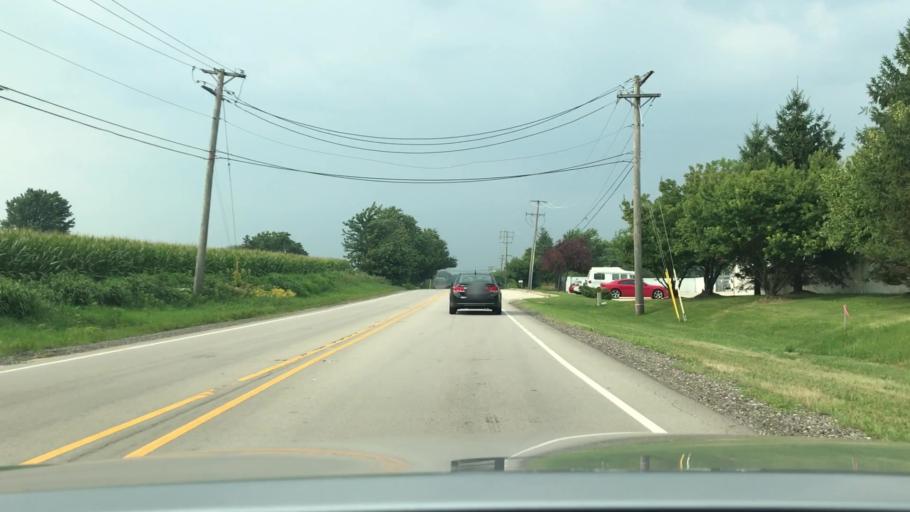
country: US
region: Illinois
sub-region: Will County
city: Plainfield
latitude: 41.6278
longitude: -88.2221
